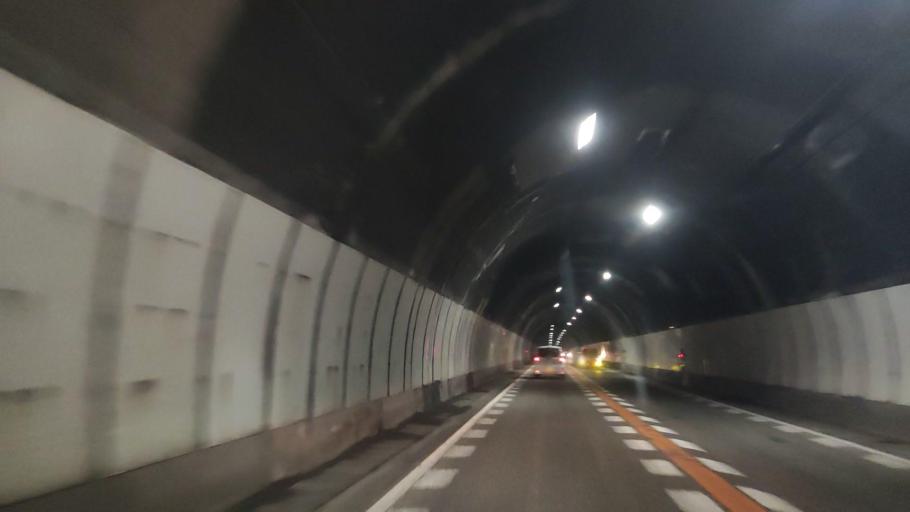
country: JP
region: Hyogo
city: Toyooka
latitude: 35.4829
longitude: 134.5815
